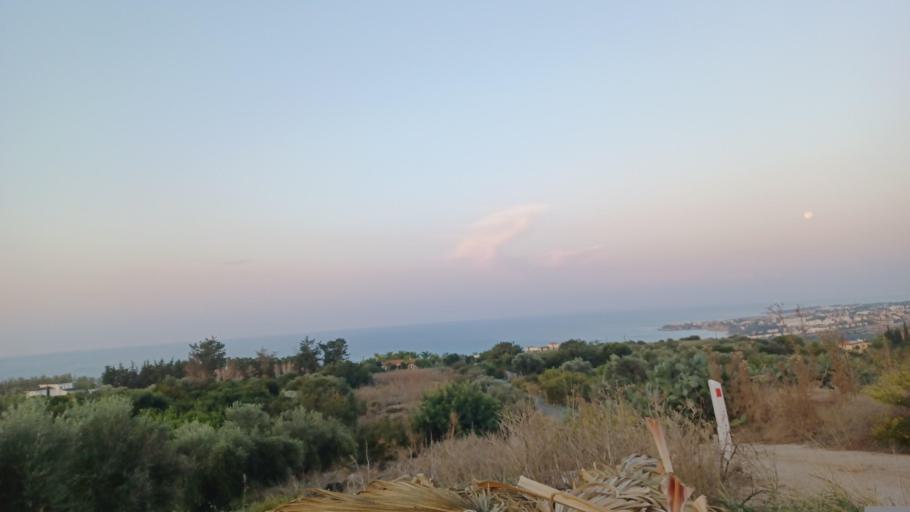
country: CY
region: Pafos
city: Kissonerga
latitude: 34.8432
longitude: 32.4048
